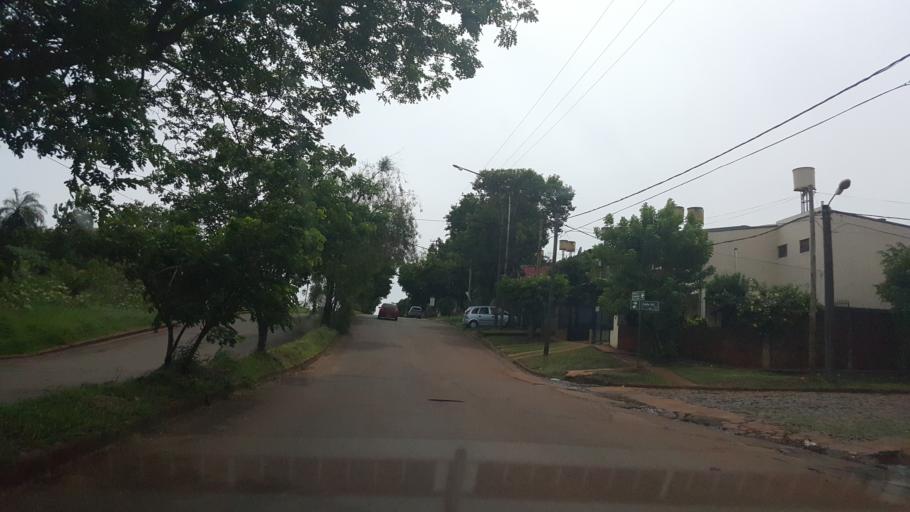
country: AR
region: Misiones
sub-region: Departamento de Capital
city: Posadas
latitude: -27.3890
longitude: -55.9423
